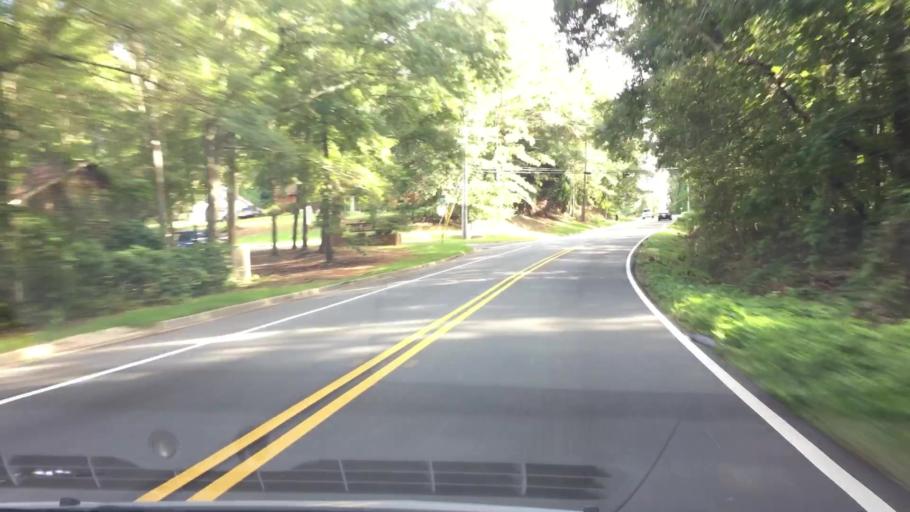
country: US
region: Georgia
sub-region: Clayton County
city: Conley
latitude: 33.6336
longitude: -84.2587
